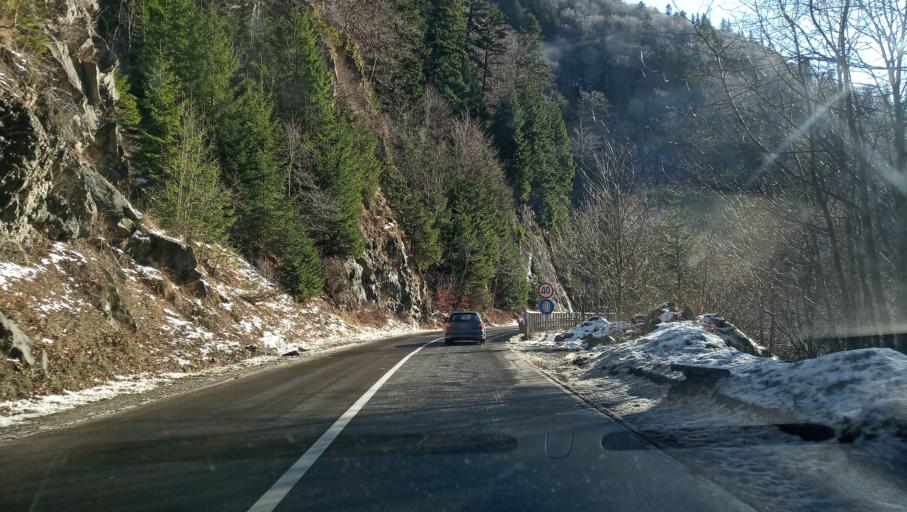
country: RO
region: Brasov
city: Crivina
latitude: 45.4753
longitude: 25.9199
